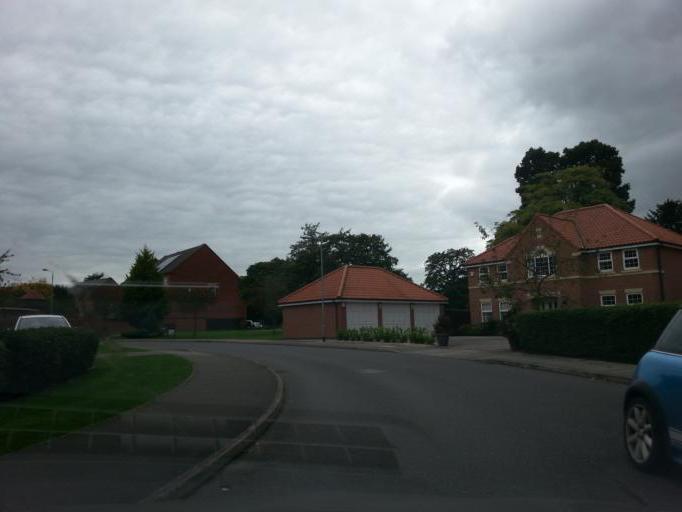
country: GB
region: England
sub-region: Lincolnshire
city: Long Bennington
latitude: 53.0449
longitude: -0.7678
